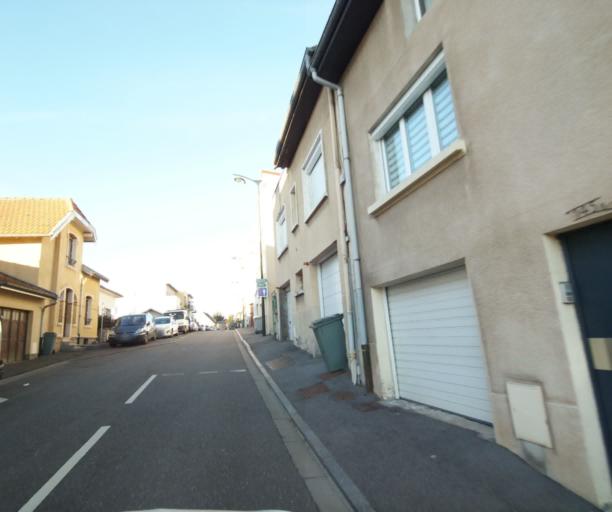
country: FR
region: Lorraine
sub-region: Departement de Meurthe-et-Moselle
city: Laxou
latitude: 48.6886
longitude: 6.1509
